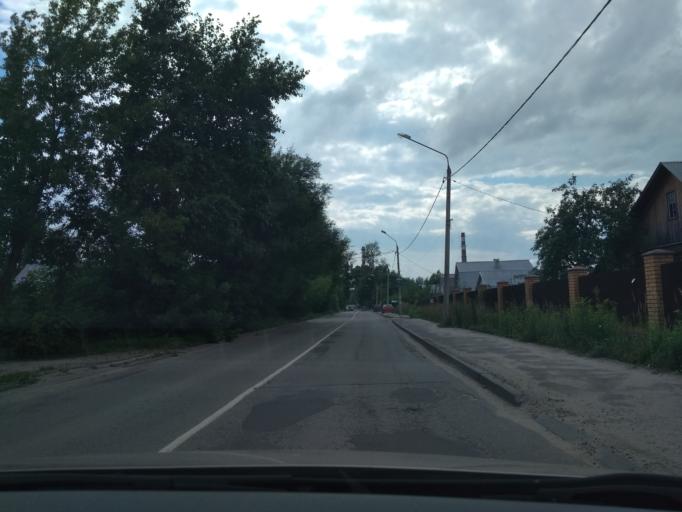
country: RU
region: Moskovskaya
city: Orekhovo-Zuyevo
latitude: 55.8019
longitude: 38.9510
